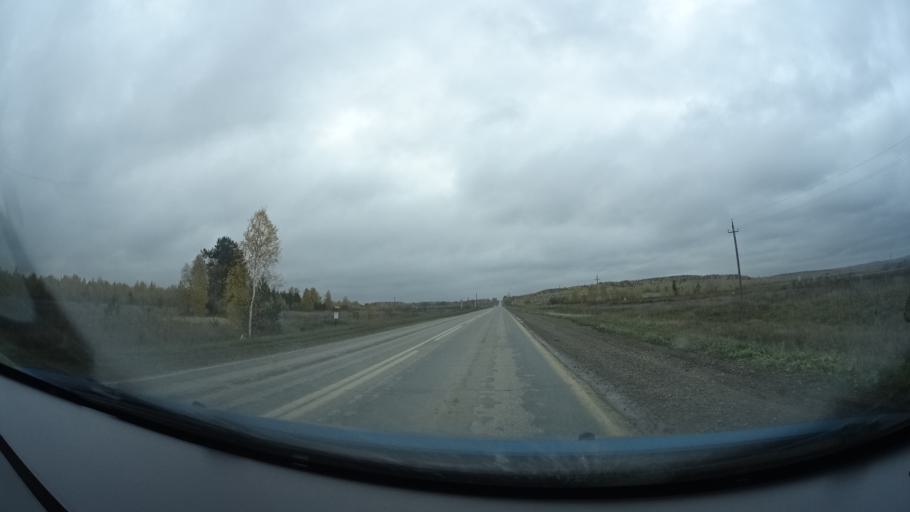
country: RU
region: Perm
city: Osa
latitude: 57.1414
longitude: 55.5283
